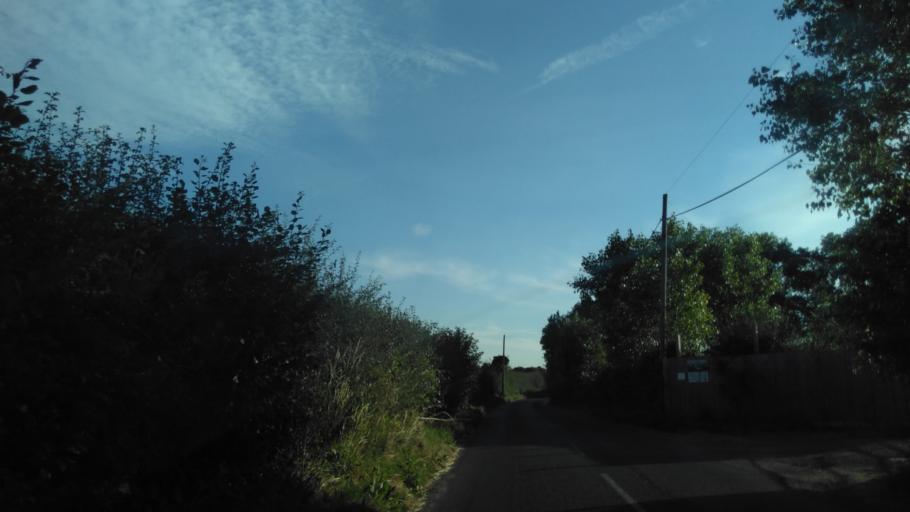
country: GB
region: England
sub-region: Kent
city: Dunkirk
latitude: 51.3197
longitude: 0.9837
